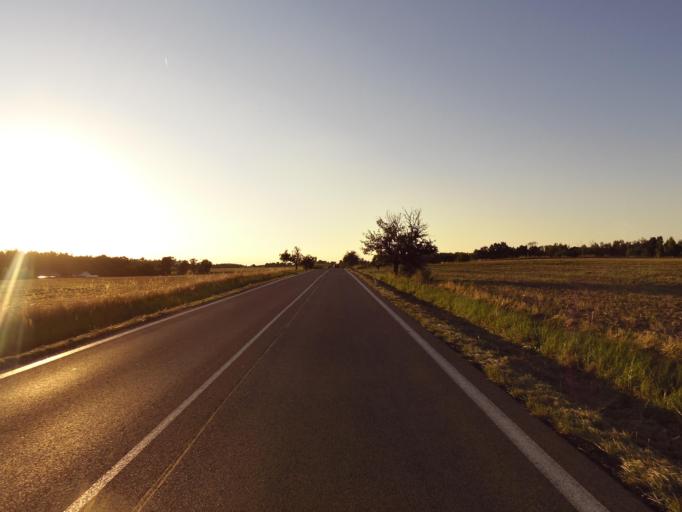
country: CZ
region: Central Bohemia
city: Mnichovo Hradiste
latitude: 50.5242
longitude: 14.9386
